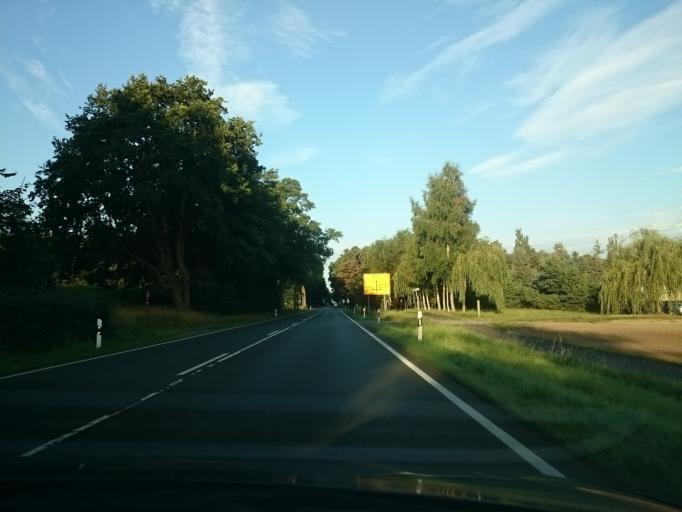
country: DE
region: Mecklenburg-Vorpommern
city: Karlshagen
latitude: 54.0641
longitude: 13.8430
